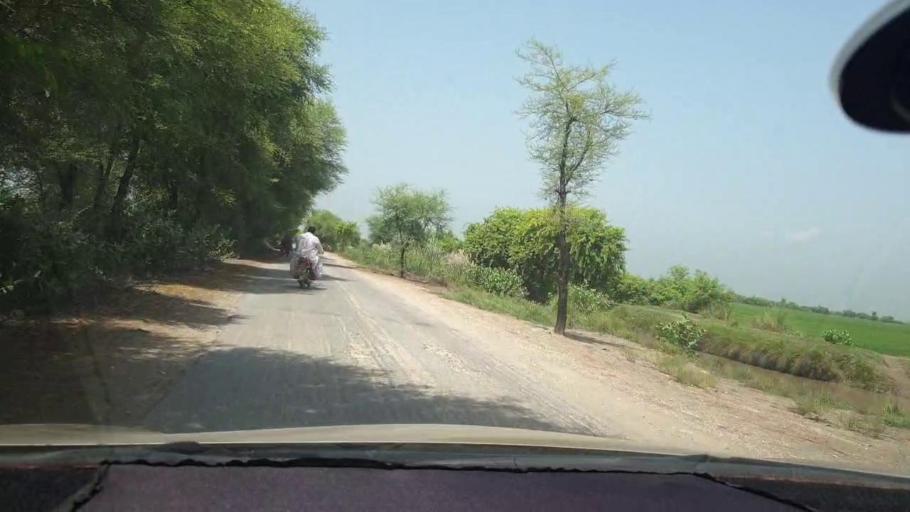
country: PK
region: Sindh
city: Kambar
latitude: 27.6385
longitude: 67.9769
